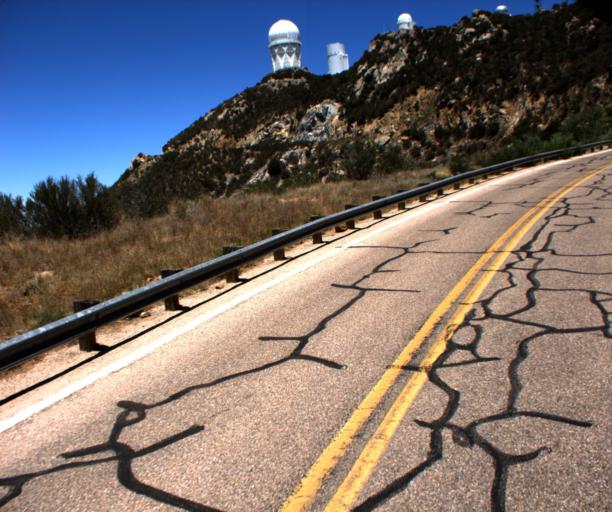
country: US
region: Arizona
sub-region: Pima County
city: Sells
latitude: 31.9592
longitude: -111.6040
